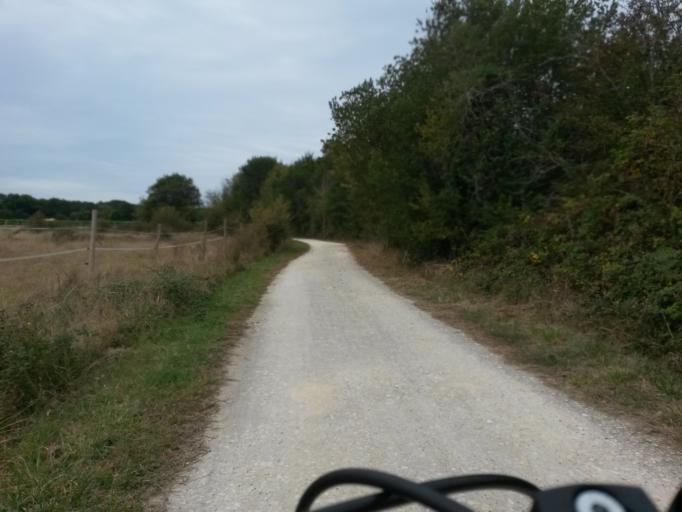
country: FR
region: Poitou-Charentes
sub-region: Departement de la Charente-Maritime
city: Dolus-d'Oleron
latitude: 45.9436
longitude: -1.3274
